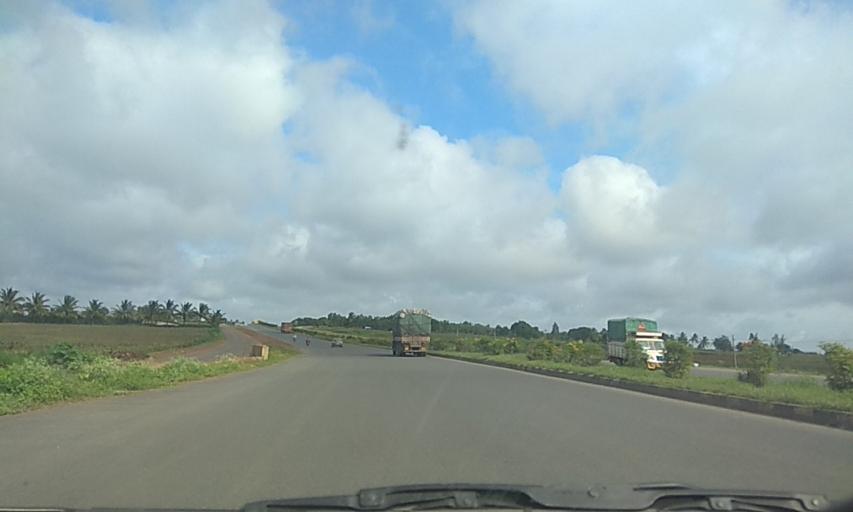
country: IN
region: Karnataka
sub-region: Haveri
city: Shiggaon
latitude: 15.0044
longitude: 75.2039
